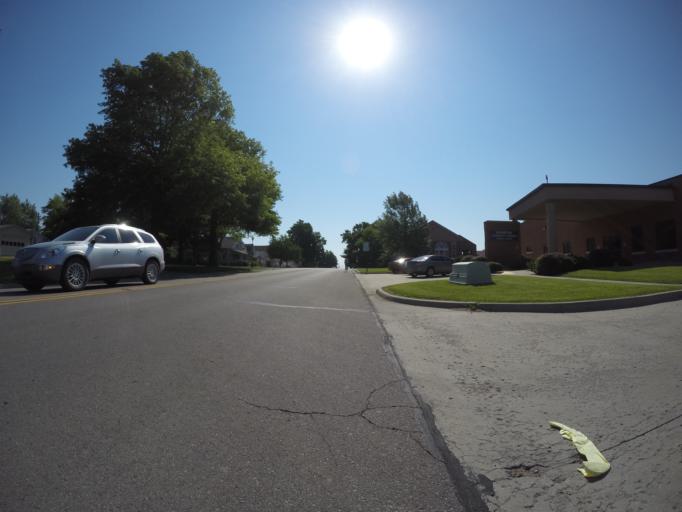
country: US
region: Kansas
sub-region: Brown County
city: Hiawatha
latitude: 39.8529
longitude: -95.5310
